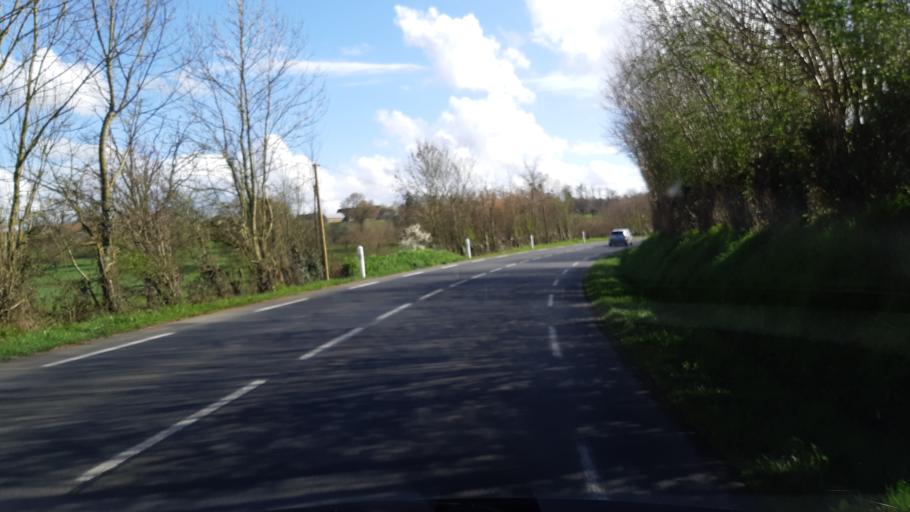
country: FR
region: Lower Normandy
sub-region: Departement de la Manche
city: Agneaux
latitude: 49.0871
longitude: -1.1144
